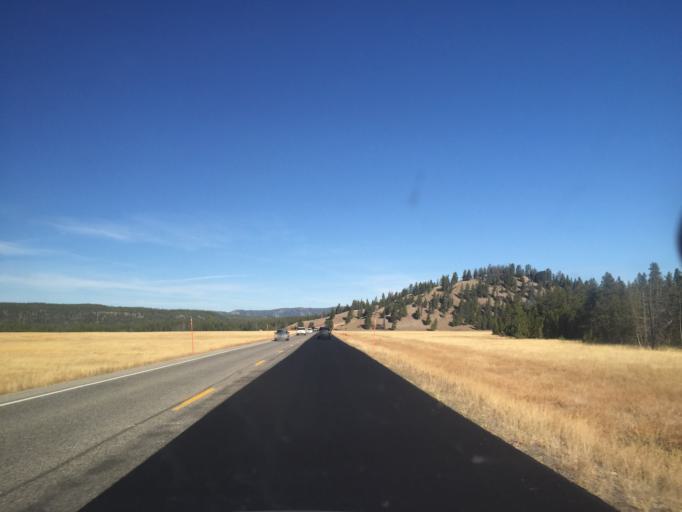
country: US
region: Montana
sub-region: Gallatin County
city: West Yellowstone
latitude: 44.5653
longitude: -110.8133
